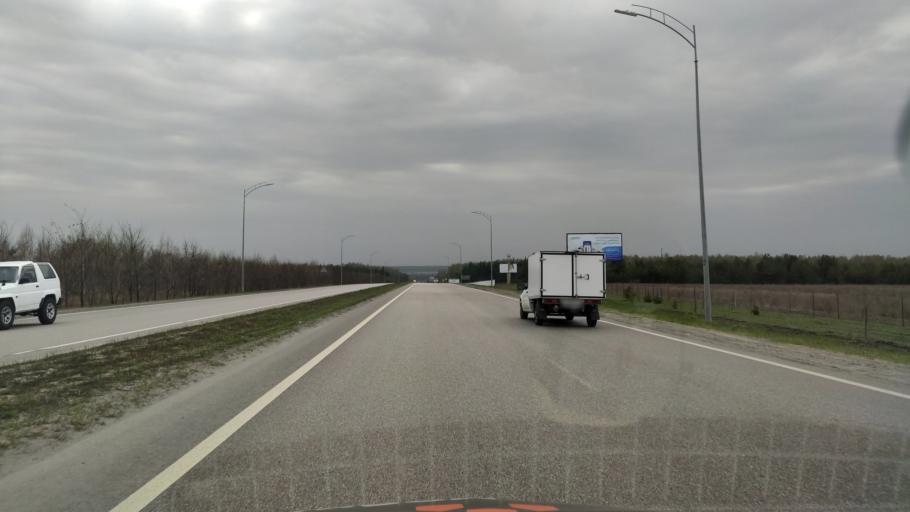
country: RU
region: Belgorod
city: Staryy Oskol
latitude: 51.3715
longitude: 37.8462
